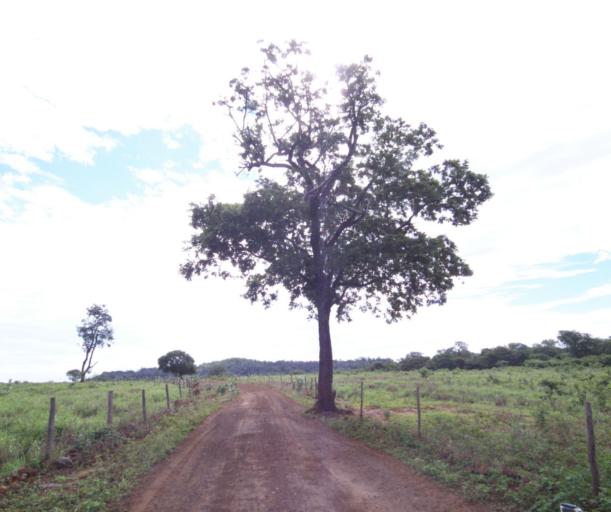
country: BR
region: Bahia
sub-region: Carinhanha
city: Carinhanha
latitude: -14.2462
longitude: -44.4214
